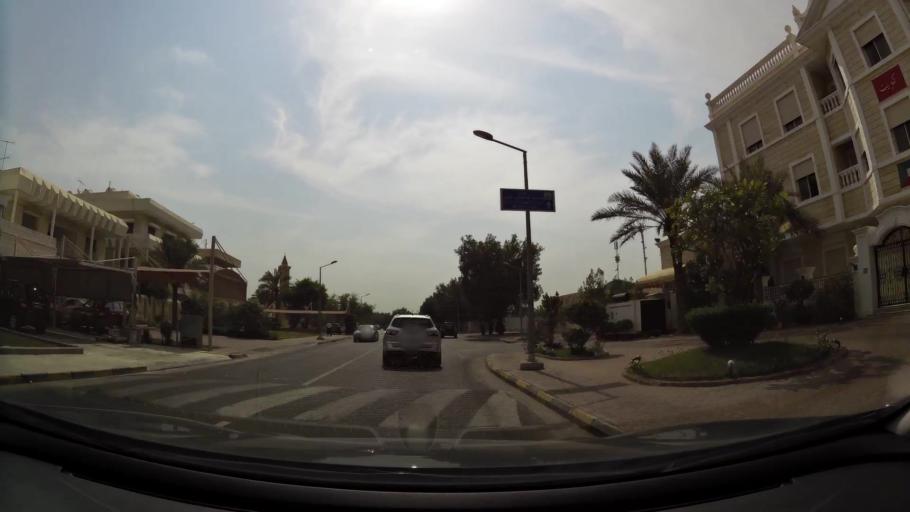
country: KW
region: Al Asimah
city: Ash Shamiyah
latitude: 29.3527
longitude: 47.9754
